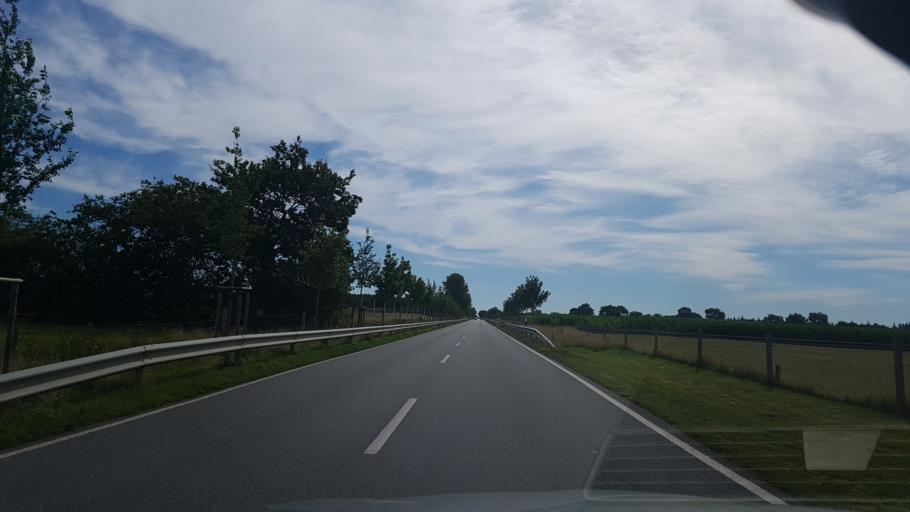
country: DE
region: Schleswig-Holstein
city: Ellhoft
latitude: 54.8883
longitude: 8.9456
